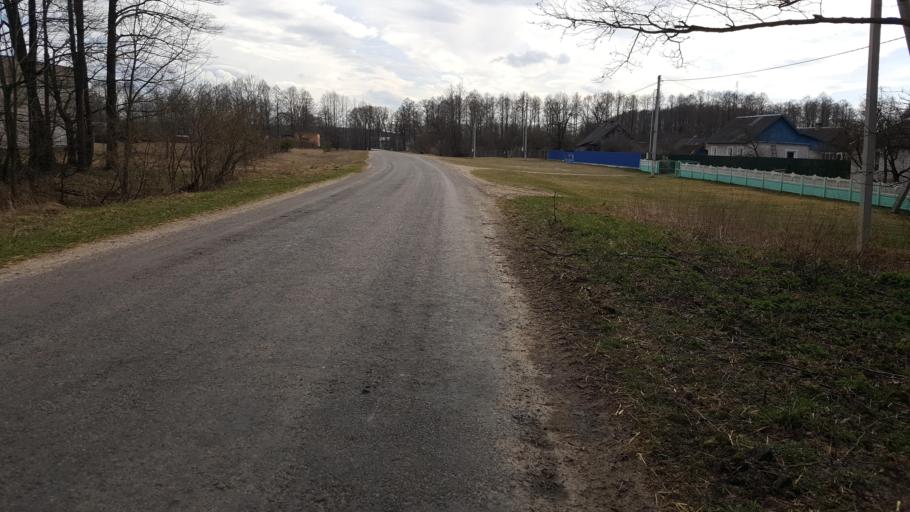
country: BY
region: Brest
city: Kamyanyets
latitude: 52.3973
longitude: 24.0039
